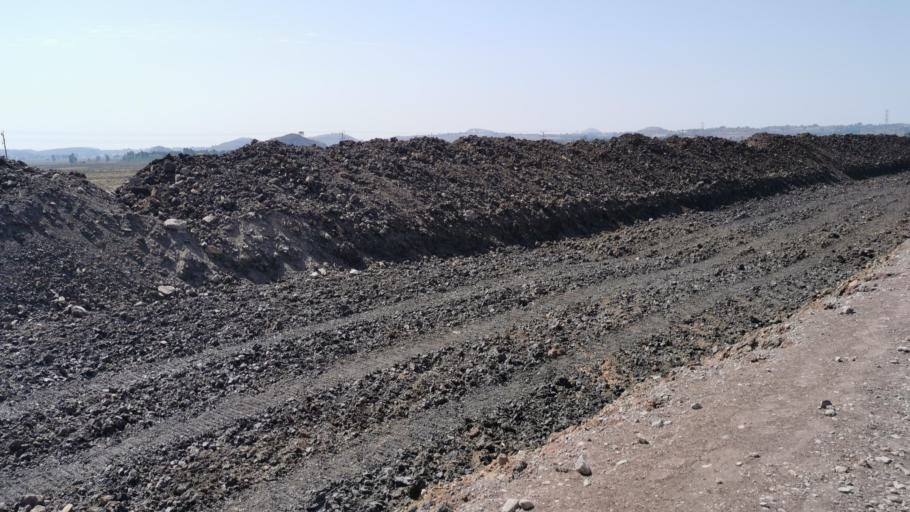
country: ET
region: Amhara
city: Bahir Dar
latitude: 11.8403
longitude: 37.0017
